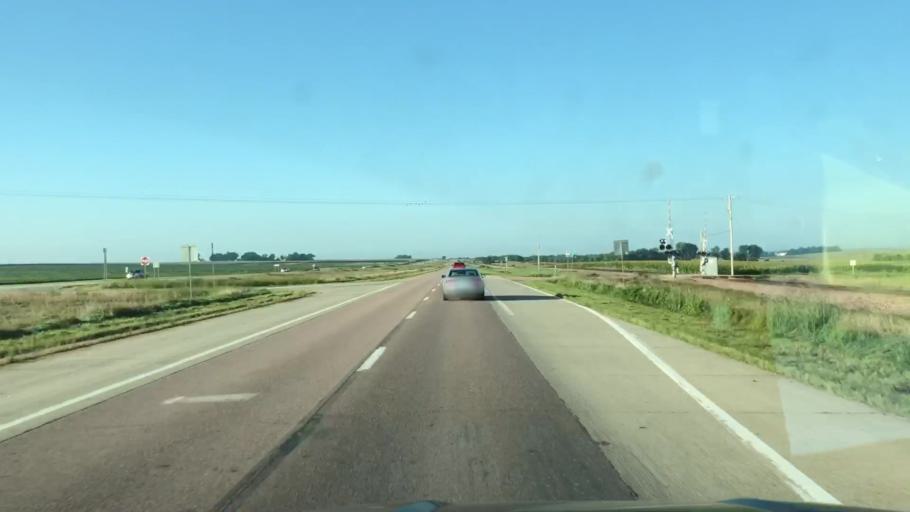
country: US
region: Iowa
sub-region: O'Brien County
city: Sheldon
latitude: 43.1279
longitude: -95.8846
